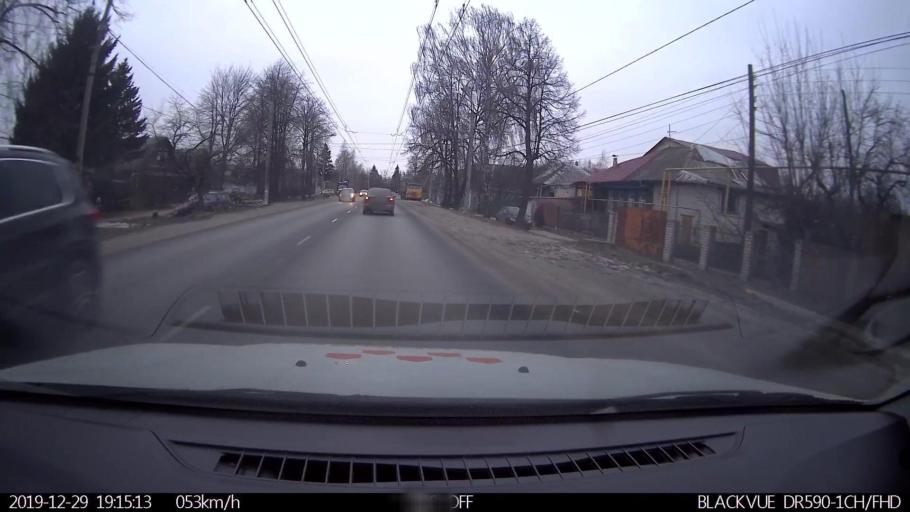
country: RU
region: Nizjnij Novgorod
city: Neklyudovo
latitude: 56.3722
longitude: 43.8391
